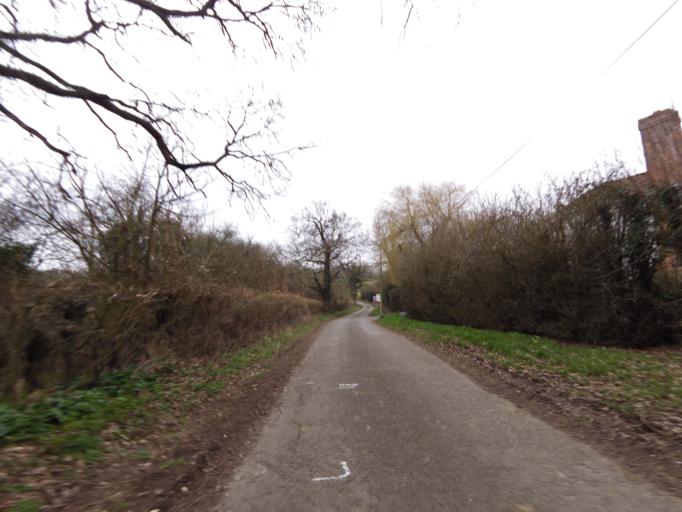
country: GB
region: England
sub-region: Suffolk
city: Framlingham
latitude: 52.2504
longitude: 1.4093
